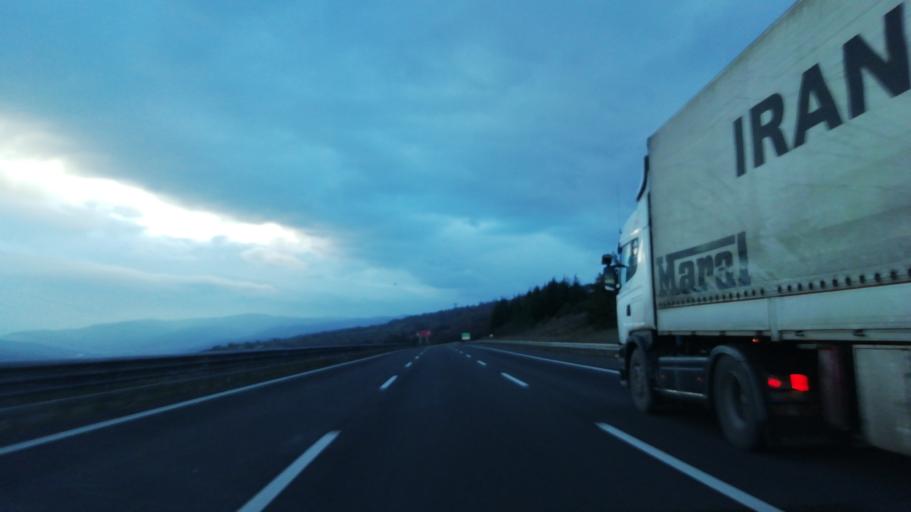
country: TR
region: Bolu
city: Bolu
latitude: 40.7323
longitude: 31.5238
